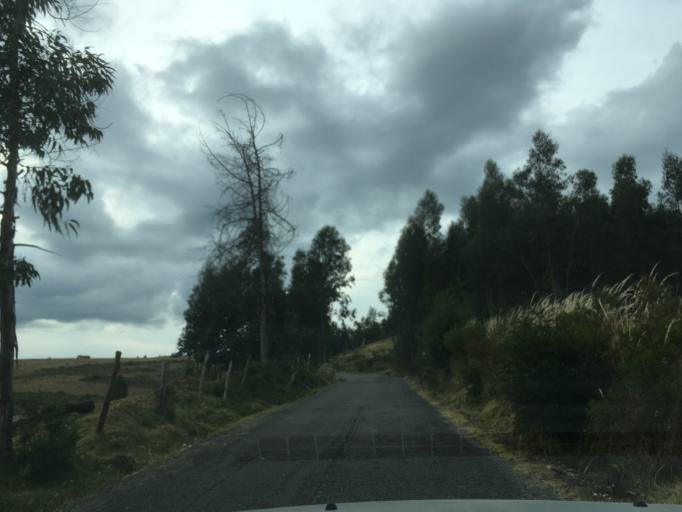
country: CO
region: Boyaca
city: Firavitoba
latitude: 5.6800
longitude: -73.0250
